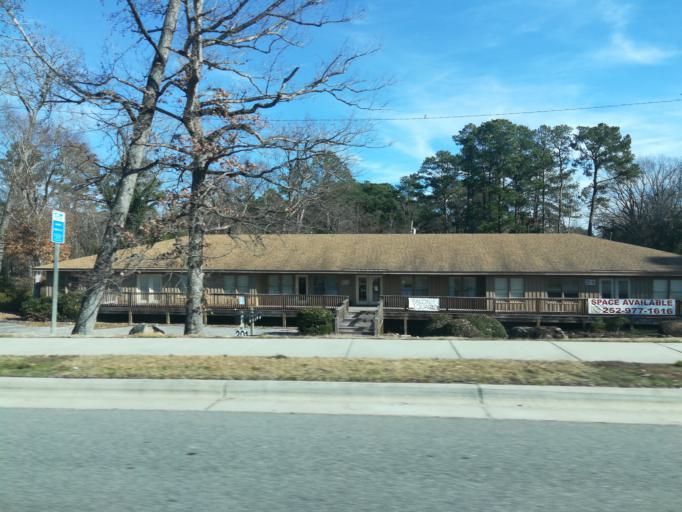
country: US
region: North Carolina
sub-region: Nash County
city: Rocky Mount
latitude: 35.9667
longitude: -77.8496
